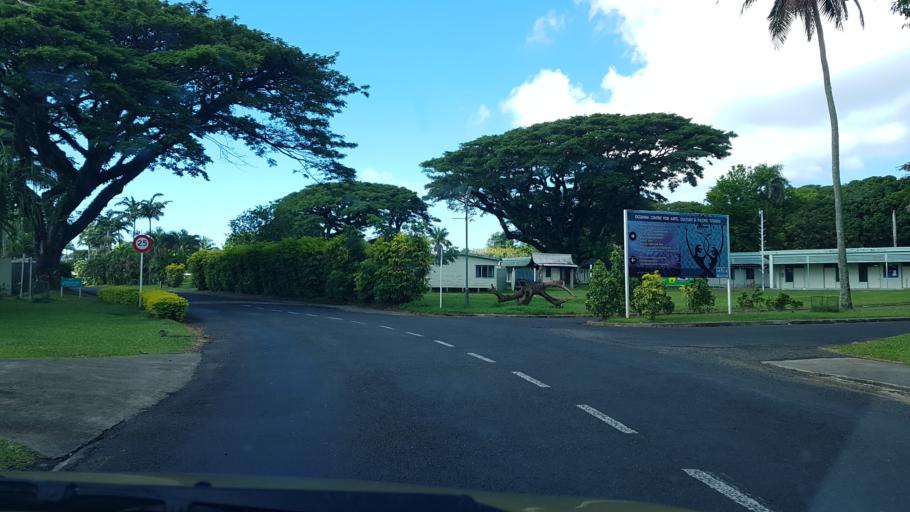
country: FJ
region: Central
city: Suva
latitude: -18.1514
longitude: 178.4436
